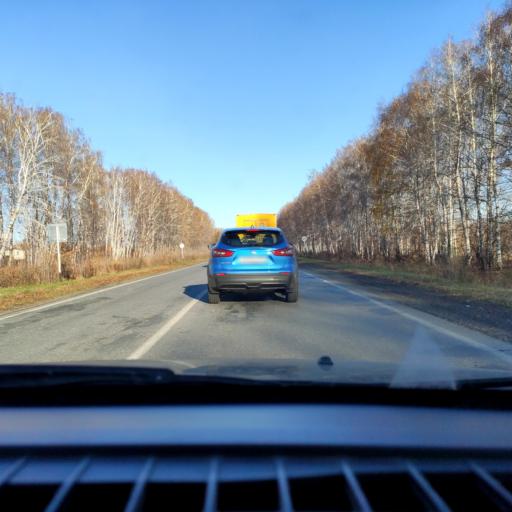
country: RU
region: Samara
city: Tol'yatti
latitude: 53.5927
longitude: 49.3279
